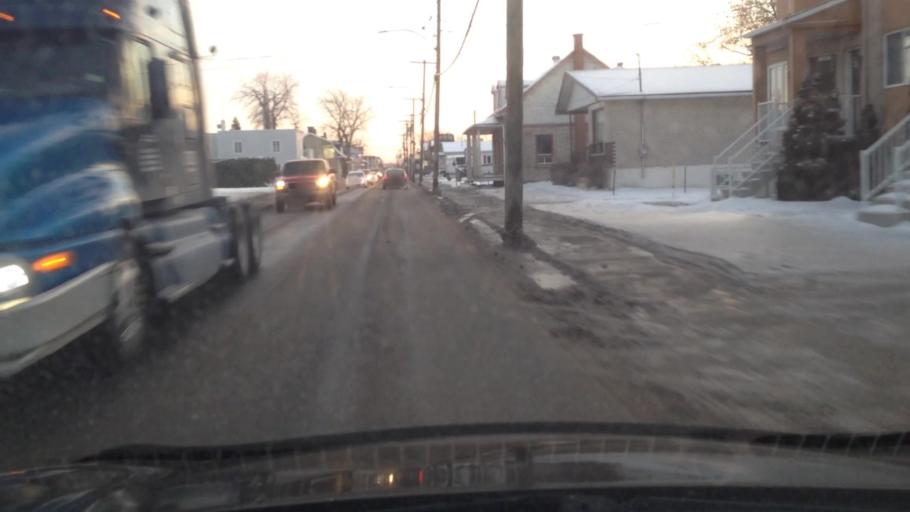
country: CA
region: Quebec
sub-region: Lanaudiere
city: Saint-Lin-Laurentides
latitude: 45.8580
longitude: -73.7571
